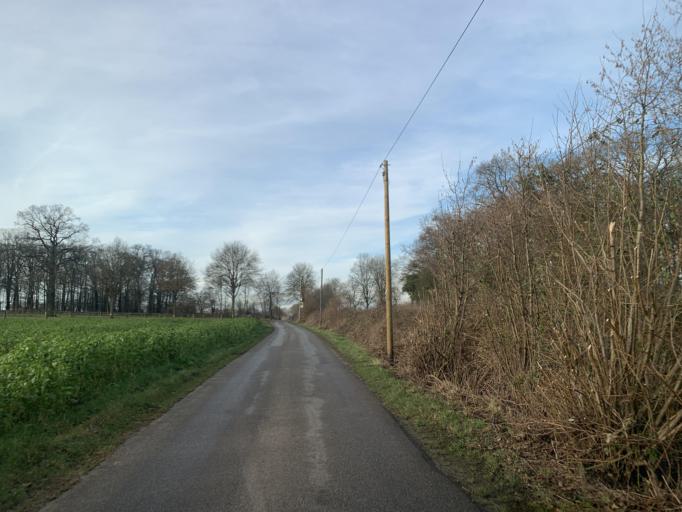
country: DE
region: North Rhine-Westphalia
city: Ludinghausen
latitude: 51.7891
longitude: 7.3898
